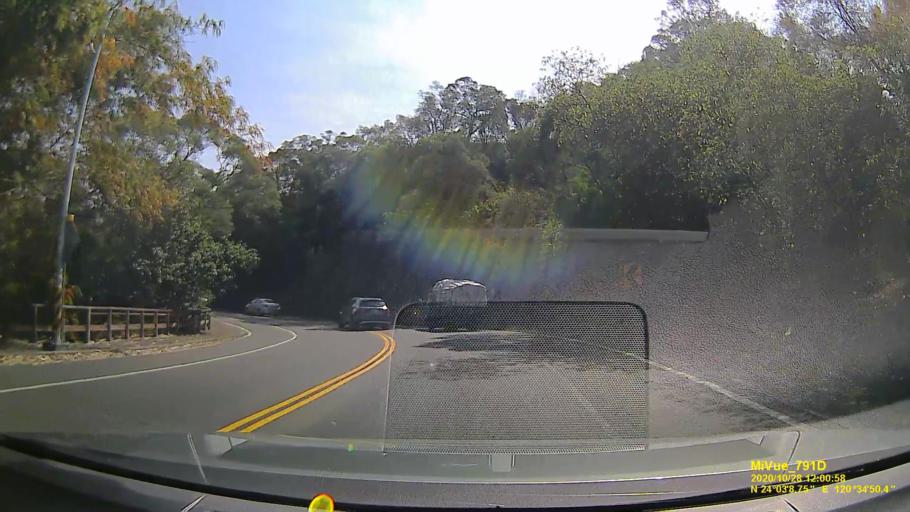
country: TW
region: Taiwan
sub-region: Changhua
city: Chang-hua
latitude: 24.0524
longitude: 120.5807
